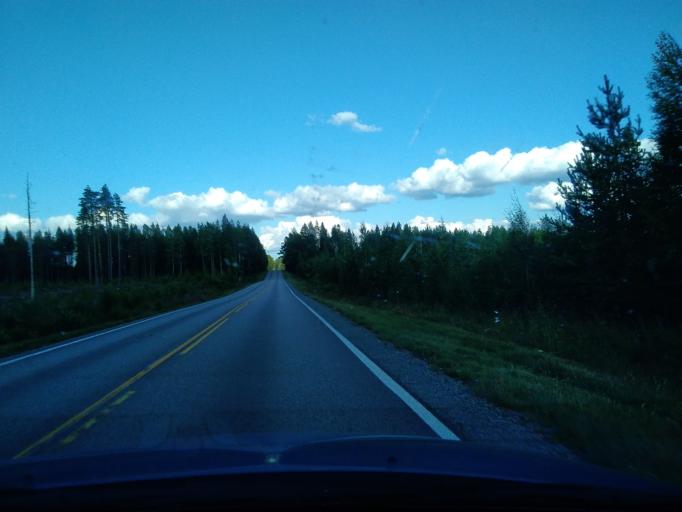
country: FI
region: Central Finland
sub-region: Saarijaervi-Viitasaari
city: Pylkoenmaeki
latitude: 62.6129
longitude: 24.7112
